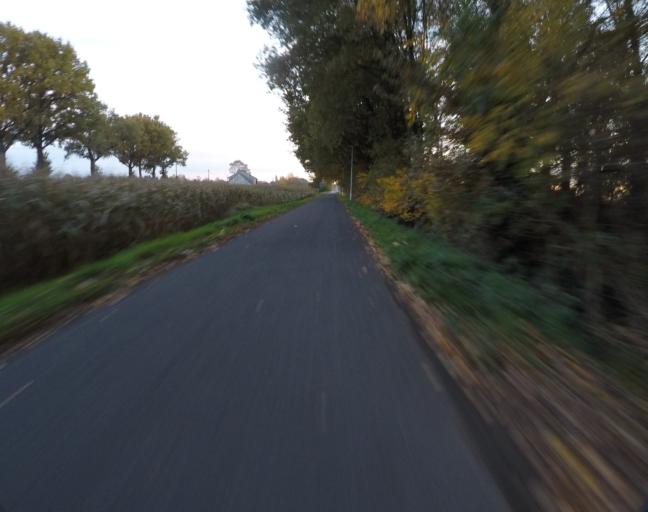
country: BE
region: Flanders
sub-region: Provincie Antwerpen
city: Olen
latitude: 51.1360
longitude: 4.8234
